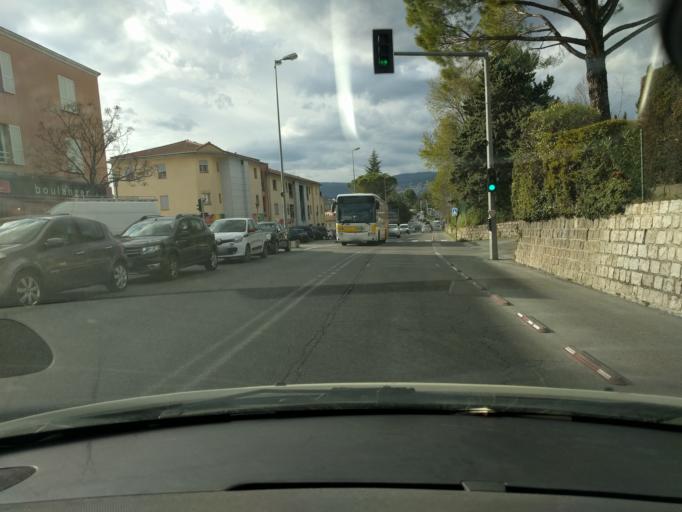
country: FR
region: Provence-Alpes-Cote d'Azur
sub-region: Departement des Alpes-Maritimes
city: Mouans-Sartoux
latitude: 43.6230
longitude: 6.9675
